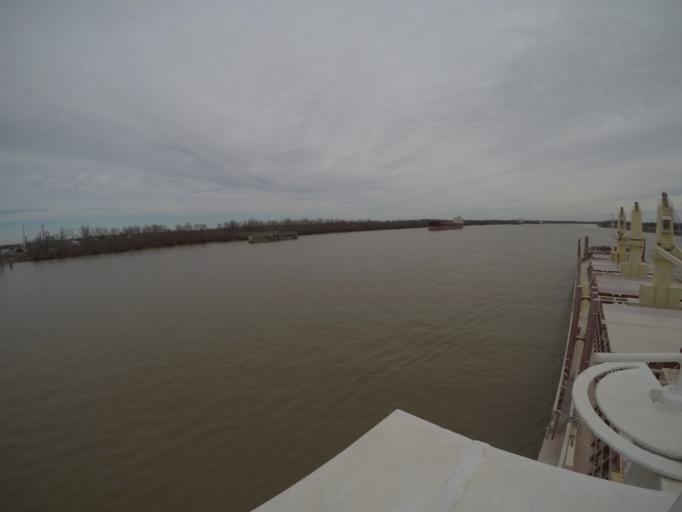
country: US
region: Louisiana
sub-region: Saint John the Baptist Parish
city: Montegut
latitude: 30.0476
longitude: -90.5204
